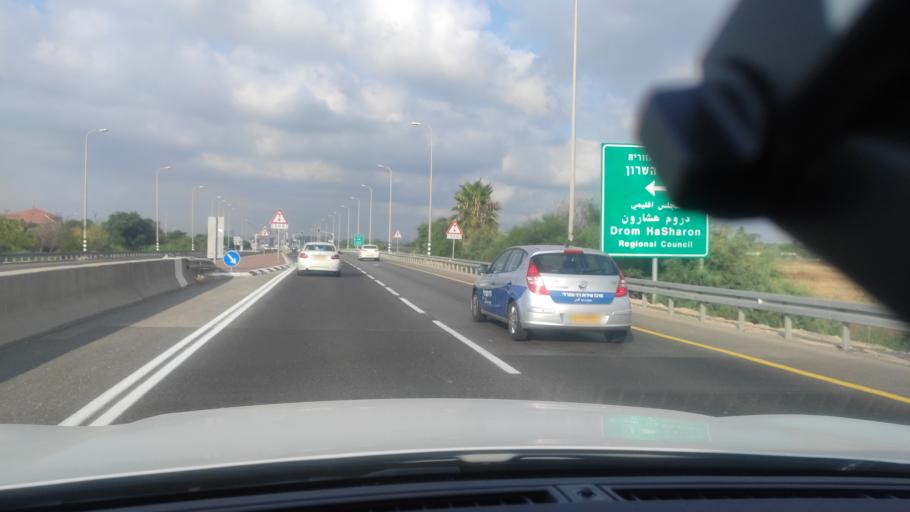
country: IL
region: Central District
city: Hod HaSharon
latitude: 32.1366
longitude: 34.9132
